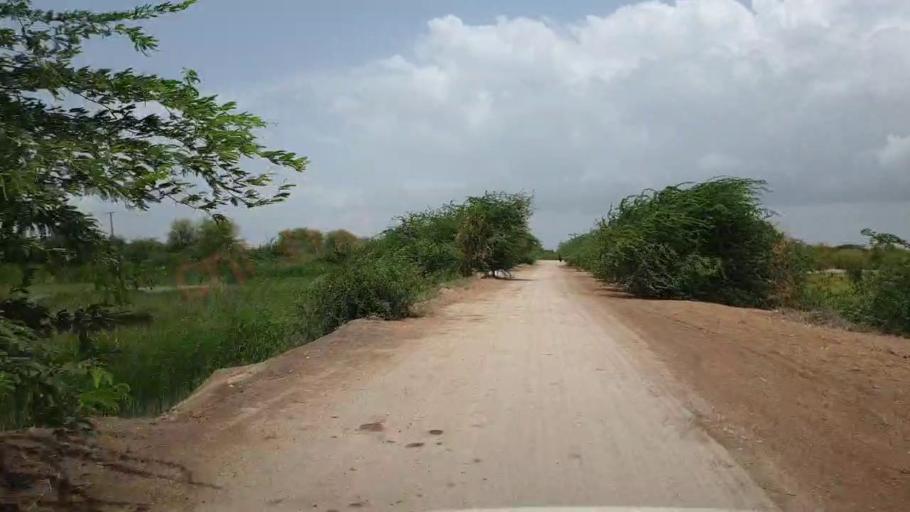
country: PK
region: Sindh
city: Kario
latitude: 24.6937
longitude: 68.6502
